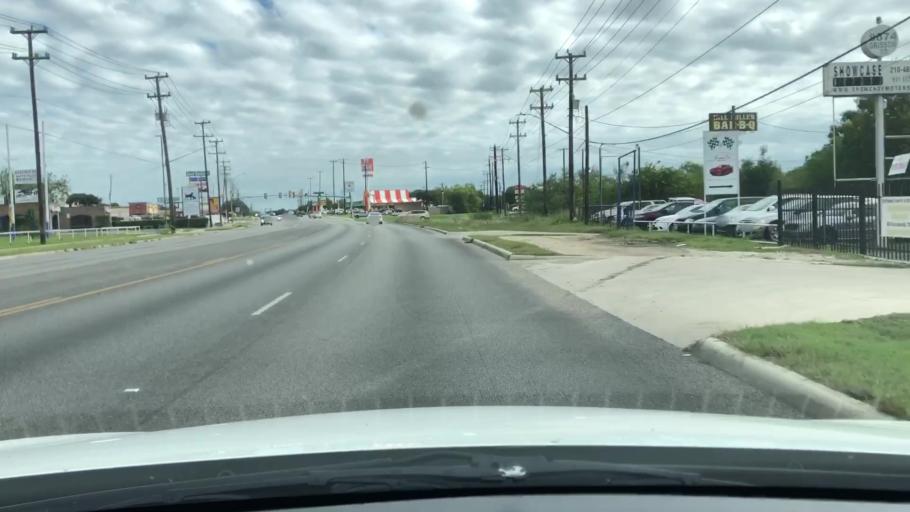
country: US
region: Texas
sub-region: Bexar County
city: Leon Valley
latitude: 29.4807
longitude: -98.6598
